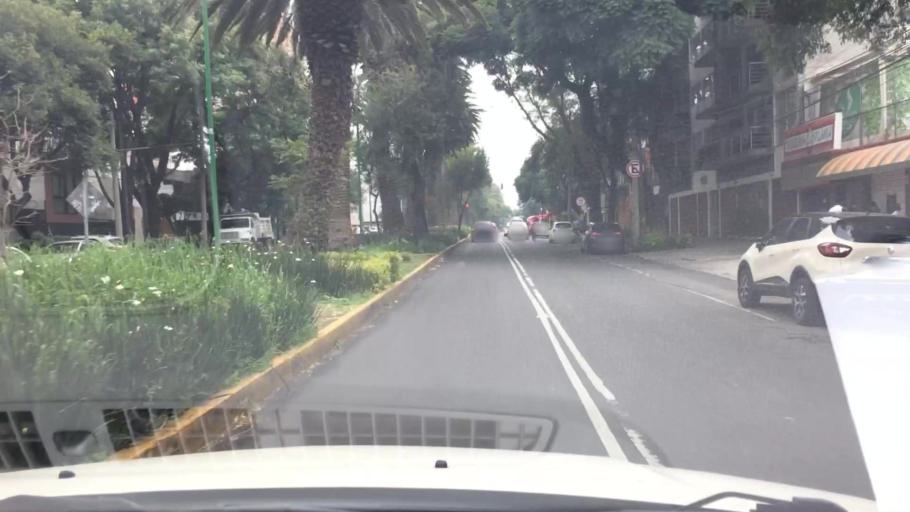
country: MX
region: Mexico City
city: Colonia del Valle
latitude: 19.3746
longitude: -99.1542
